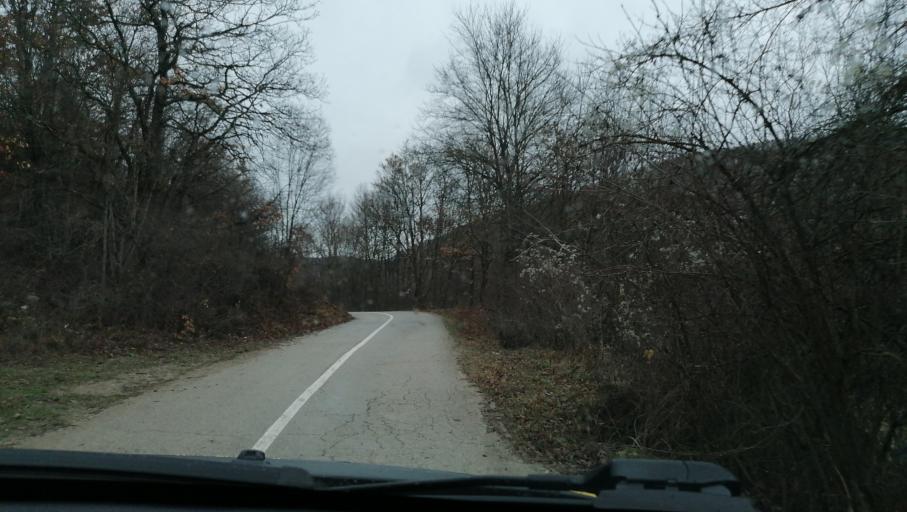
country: RS
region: Central Serbia
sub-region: Pirotski Okrug
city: Dimitrovgrad
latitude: 42.9662
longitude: 22.7838
